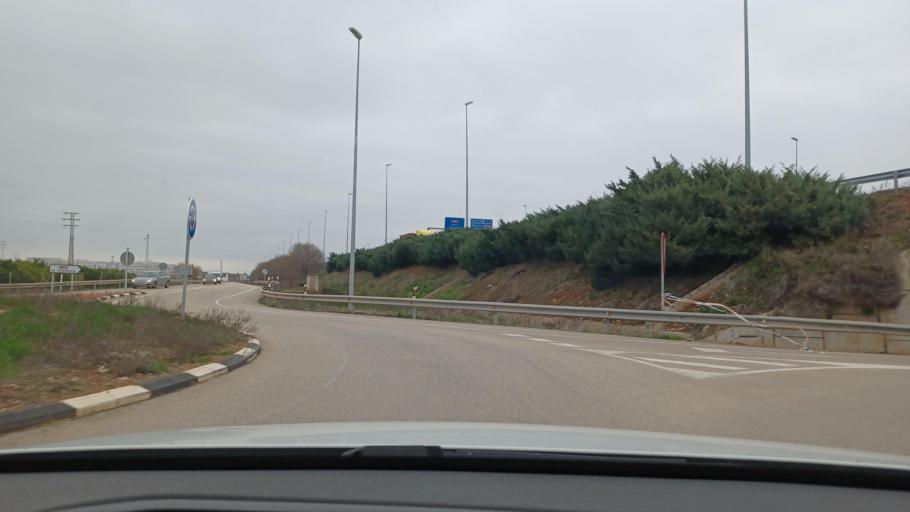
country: ES
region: Valencia
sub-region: Provincia de Castello
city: Villavieja
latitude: 39.8519
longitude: -0.1734
